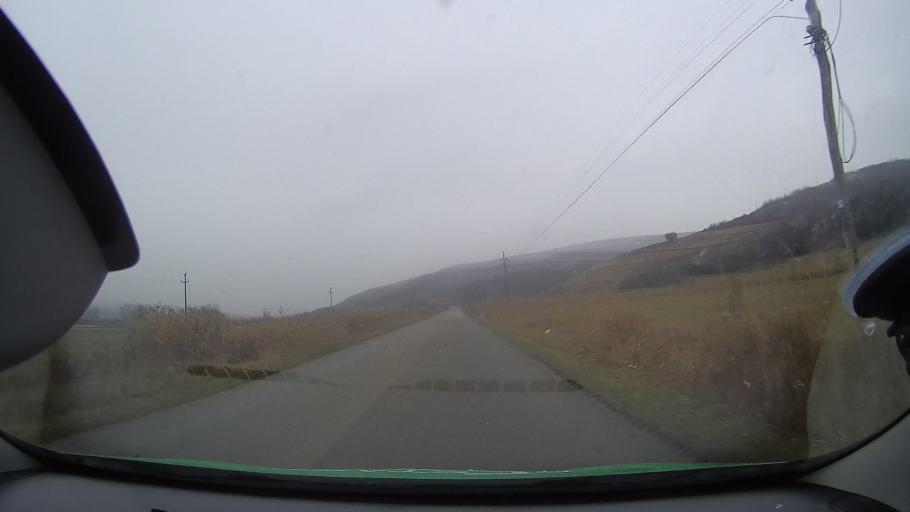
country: RO
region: Alba
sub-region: Comuna Farau
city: Farau
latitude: 46.3392
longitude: 23.9909
